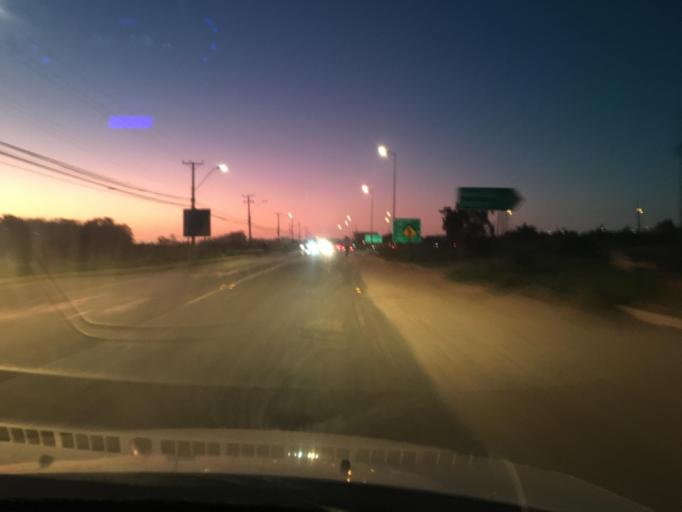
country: CL
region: Valparaiso
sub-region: San Antonio Province
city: El Tabo
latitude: -33.4257
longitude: -71.6916
